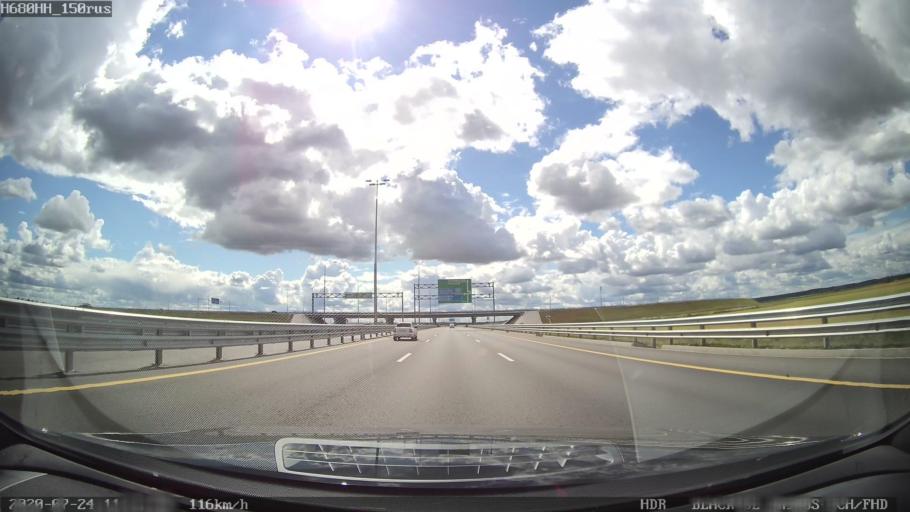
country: RU
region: St.-Petersburg
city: Tyarlevo
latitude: 59.7297
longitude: 30.5099
